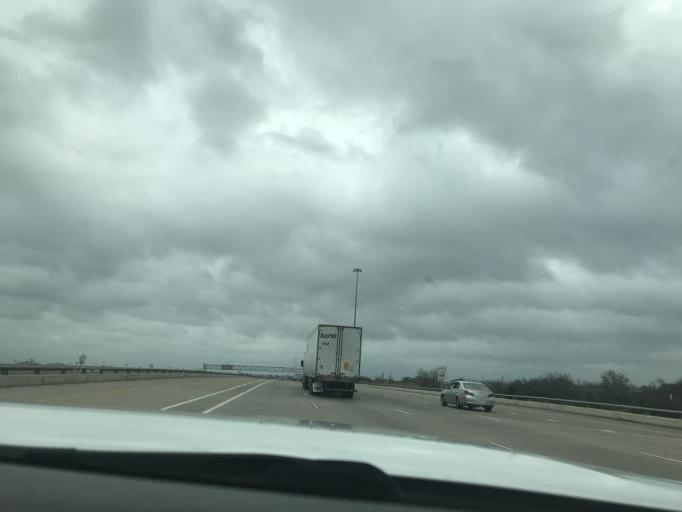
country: US
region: Texas
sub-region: Fort Bend County
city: Greatwood
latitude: 29.5612
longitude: -95.6910
